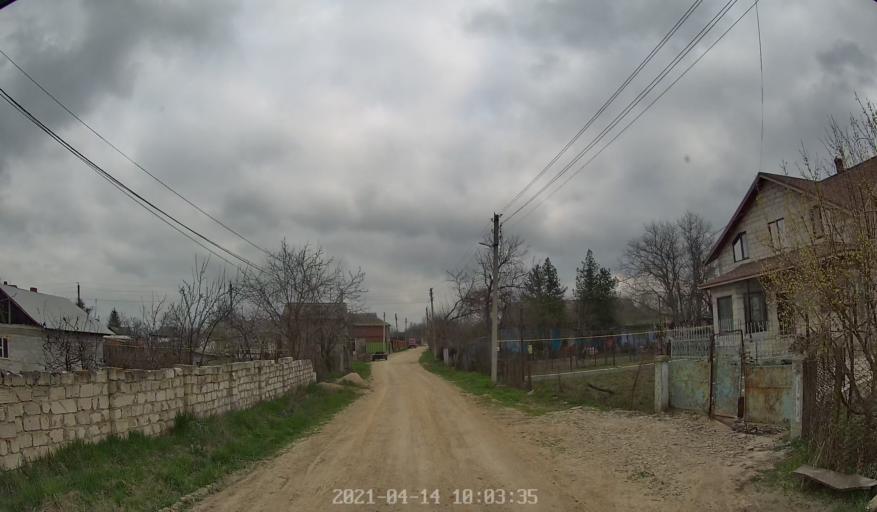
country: MD
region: Chisinau
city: Vadul lui Voda
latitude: 47.1437
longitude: 29.1249
